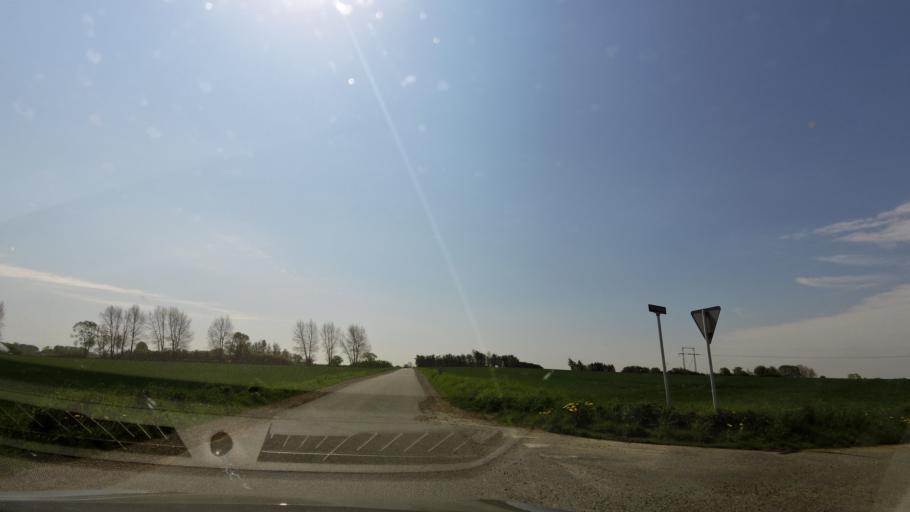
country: DK
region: South Denmark
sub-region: Nyborg Kommune
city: Ullerslev
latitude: 55.2670
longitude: 10.6919
